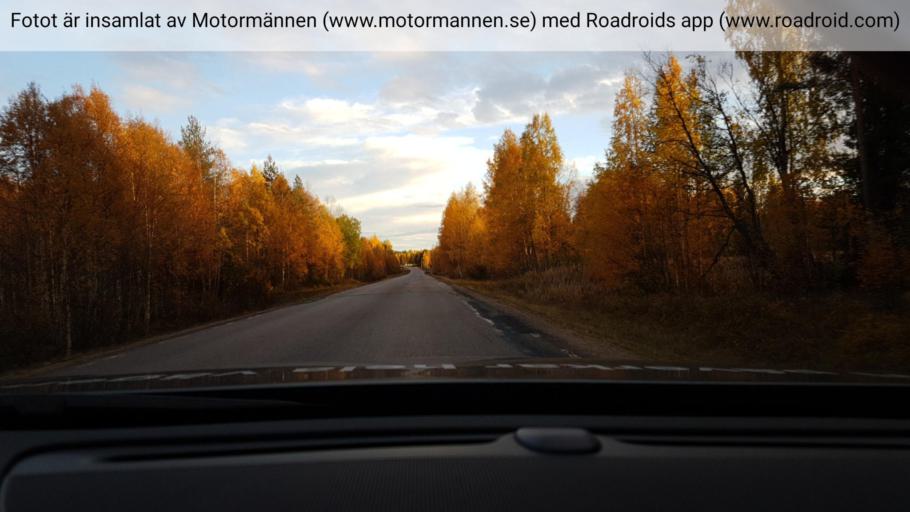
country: SE
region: Norrbotten
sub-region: Overkalix Kommun
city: OEverkalix
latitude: 66.6311
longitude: 22.7320
